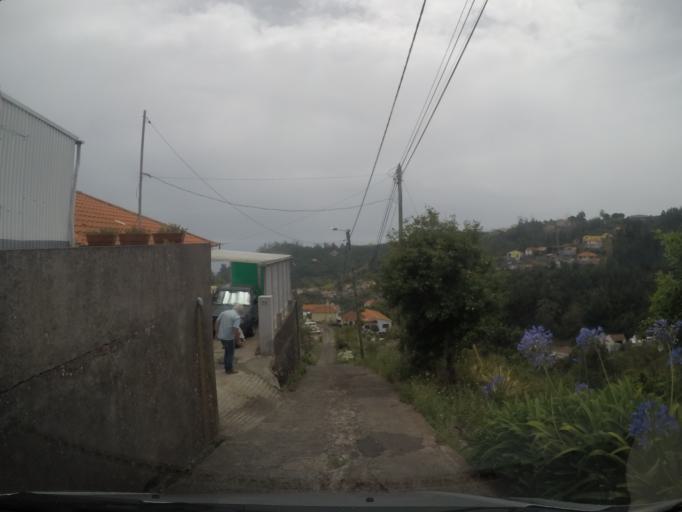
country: PT
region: Madeira
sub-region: Santa Cruz
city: Camacha
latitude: 32.6763
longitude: -16.8396
